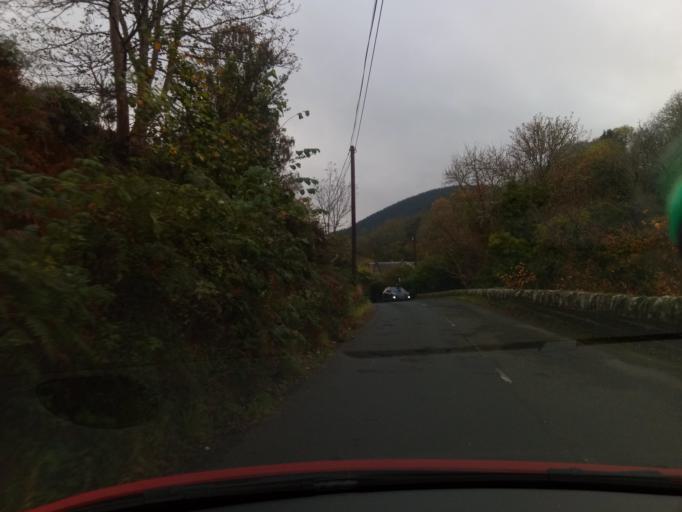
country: GB
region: Scotland
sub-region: The Scottish Borders
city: Galashiels
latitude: 55.6113
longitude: -2.8767
